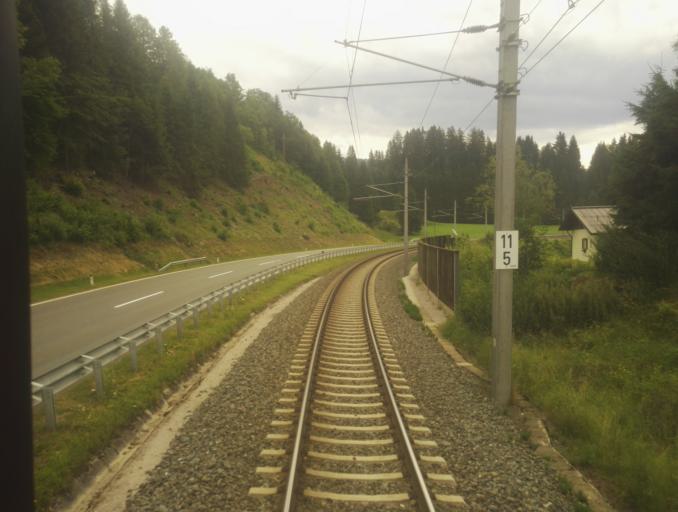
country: AT
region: Salzburg
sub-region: Politischer Bezirk Sankt Johann im Pongau
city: Huttau
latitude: 47.4226
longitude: 13.3359
